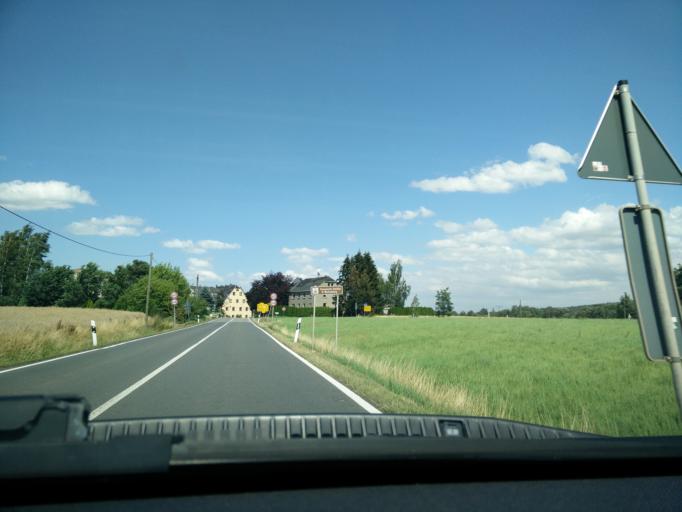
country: DE
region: Saxony
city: Narsdorf
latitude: 51.0165
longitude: 12.7305
